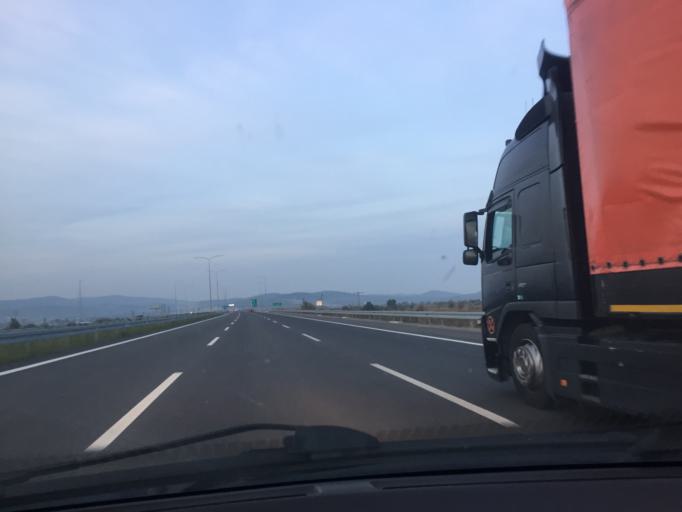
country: TR
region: Manisa
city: Halitpasa
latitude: 38.7553
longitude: 27.6603
